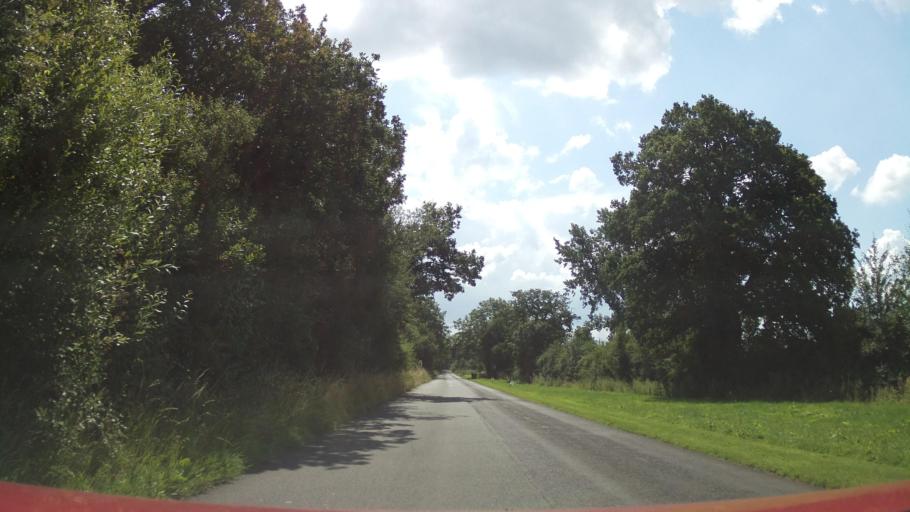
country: GB
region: England
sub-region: Wiltshire
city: Minety
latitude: 51.5948
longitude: -1.9368
